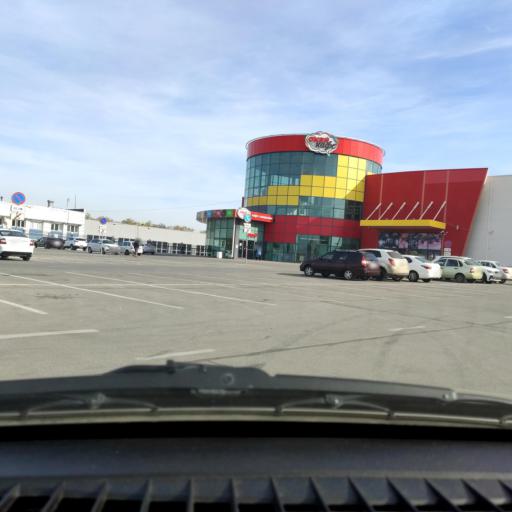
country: RU
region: Samara
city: Tol'yatti
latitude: 53.5435
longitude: 49.2863
